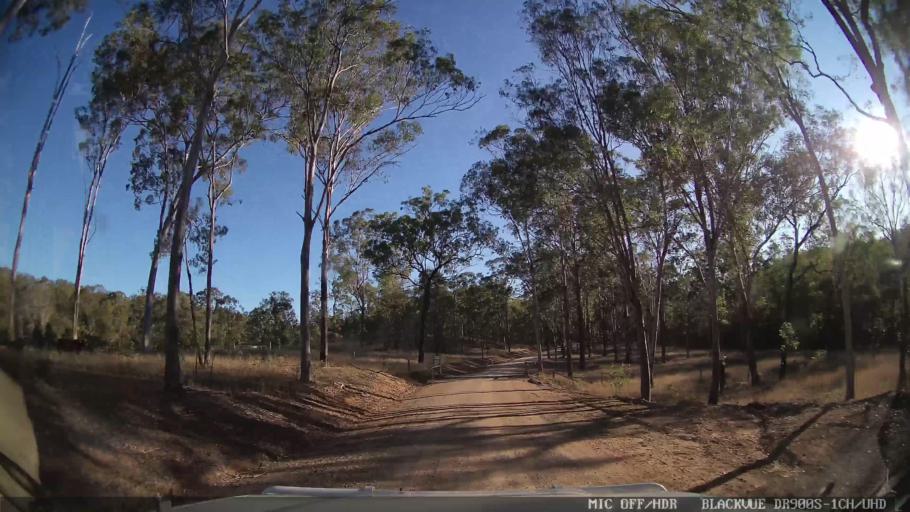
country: AU
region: Queensland
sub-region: Gladstone
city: Toolooa
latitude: -24.6945
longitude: 151.4121
